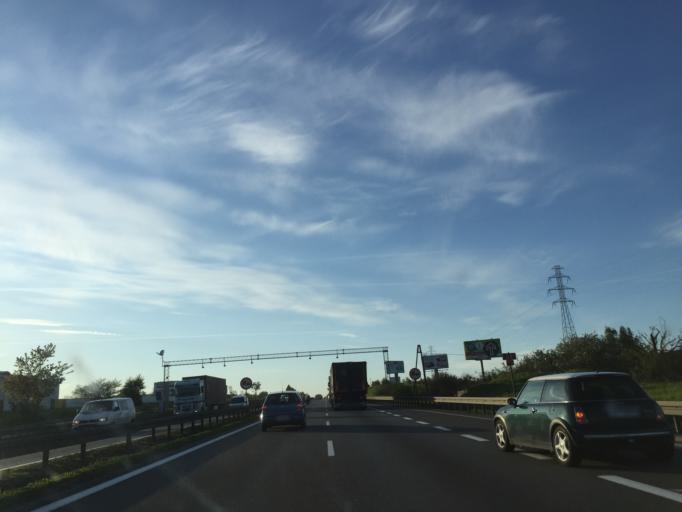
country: PL
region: Pomeranian Voivodeship
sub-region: Powiat gdanski
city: Kowale
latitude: 54.3279
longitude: 18.5395
